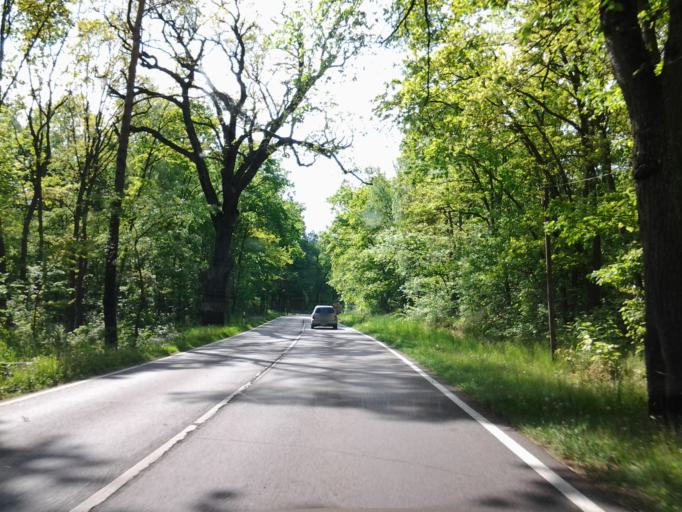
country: DE
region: Brandenburg
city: Oranienburg
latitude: 52.7652
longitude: 13.2848
